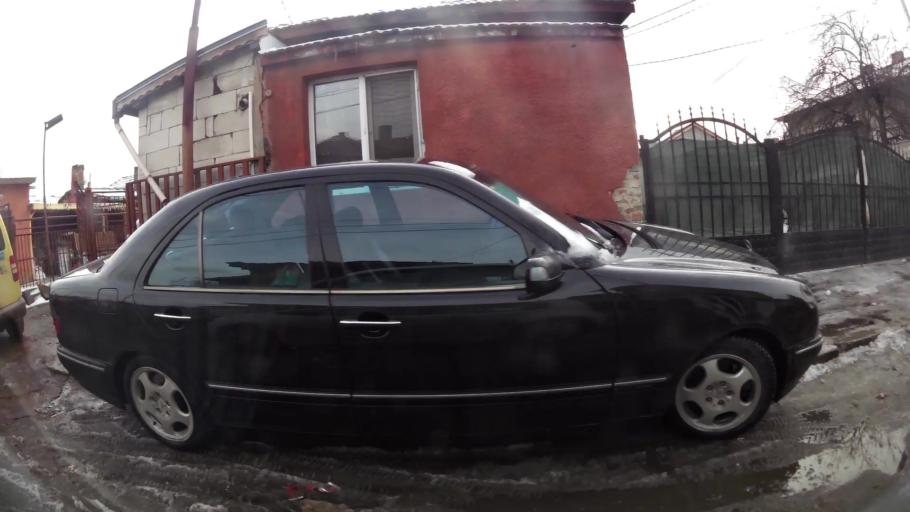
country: BG
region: Sofia-Capital
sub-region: Stolichna Obshtina
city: Sofia
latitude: 42.6869
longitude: 23.3828
